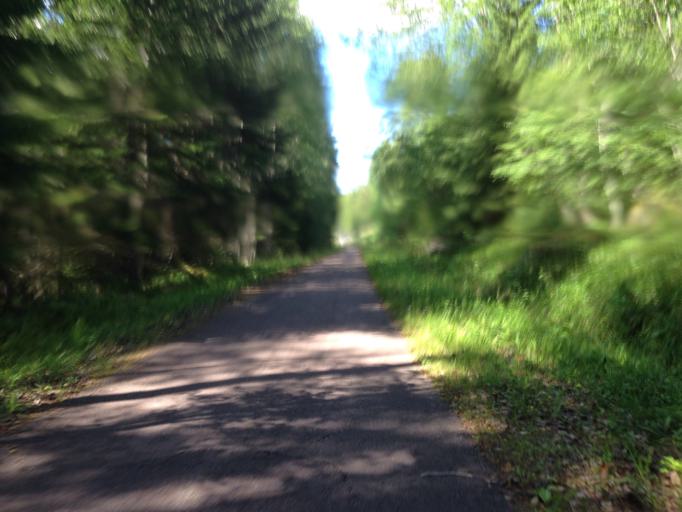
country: SE
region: Dalarna
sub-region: Ludvika Kommun
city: Grangesberg
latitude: 60.2102
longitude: 15.0502
